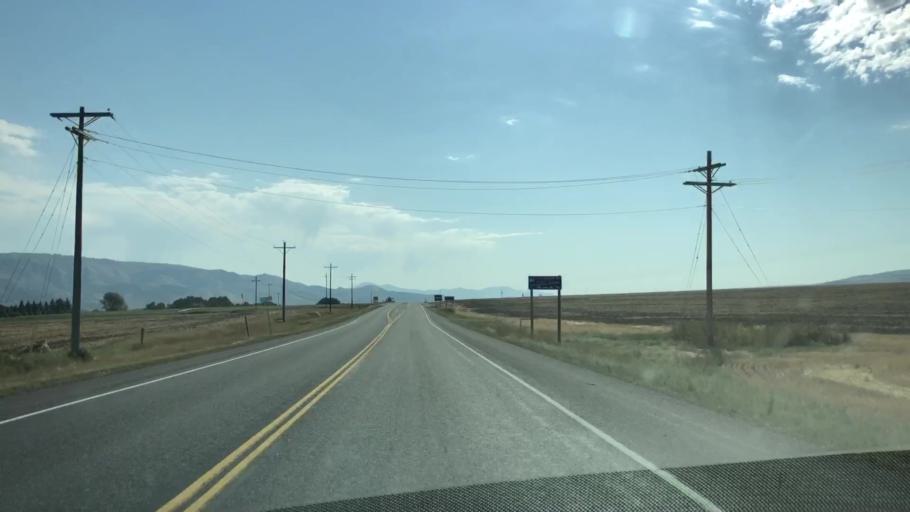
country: US
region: Idaho
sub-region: Jefferson County
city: Rigby
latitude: 43.6123
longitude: -111.7190
